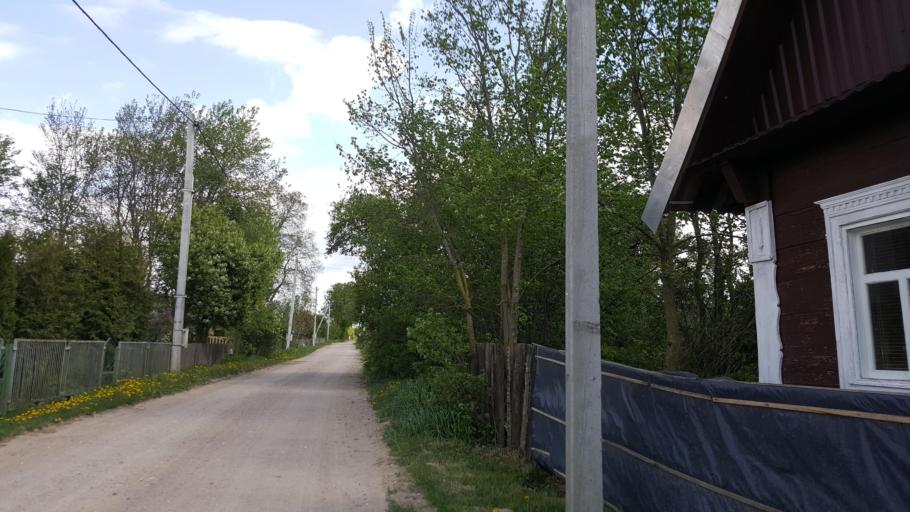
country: BY
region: Brest
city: Kamyanyets
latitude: 52.3865
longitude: 23.8844
